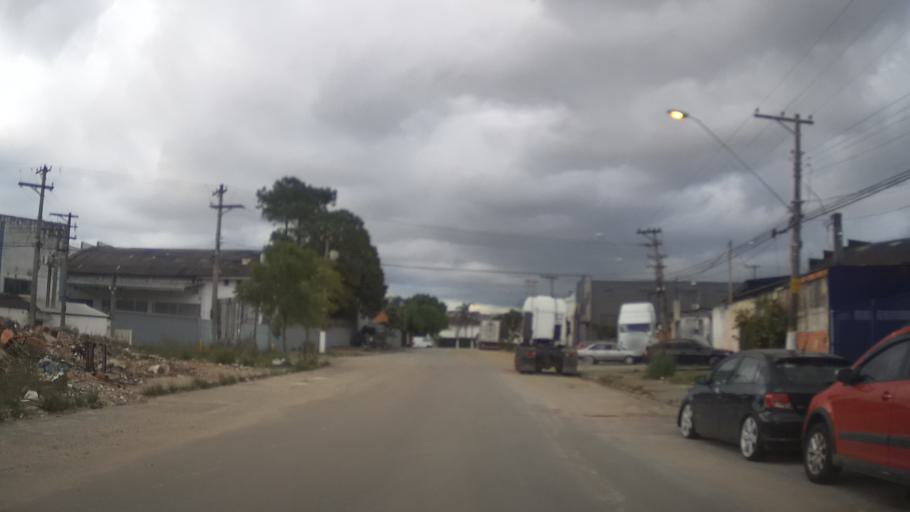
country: BR
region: Sao Paulo
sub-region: Guarulhos
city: Guarulhos
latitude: -23.4608
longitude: -46.4745
